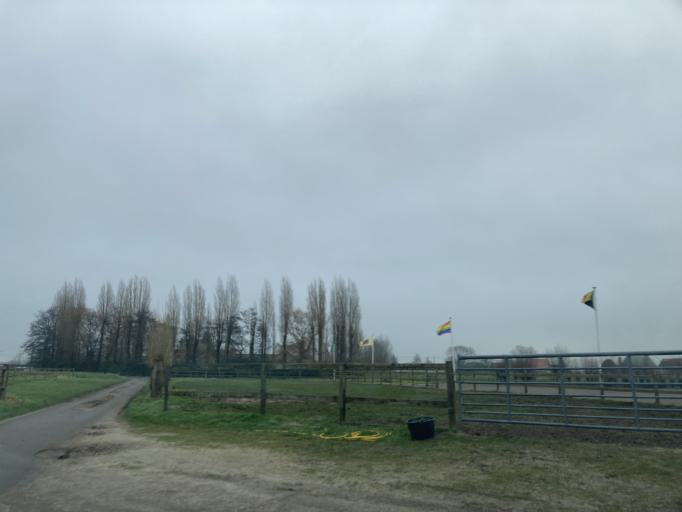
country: BE
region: Flanders
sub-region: Provincie West-Vlaanderen
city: Oudenburg
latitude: 51.1457
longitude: 3.0217
